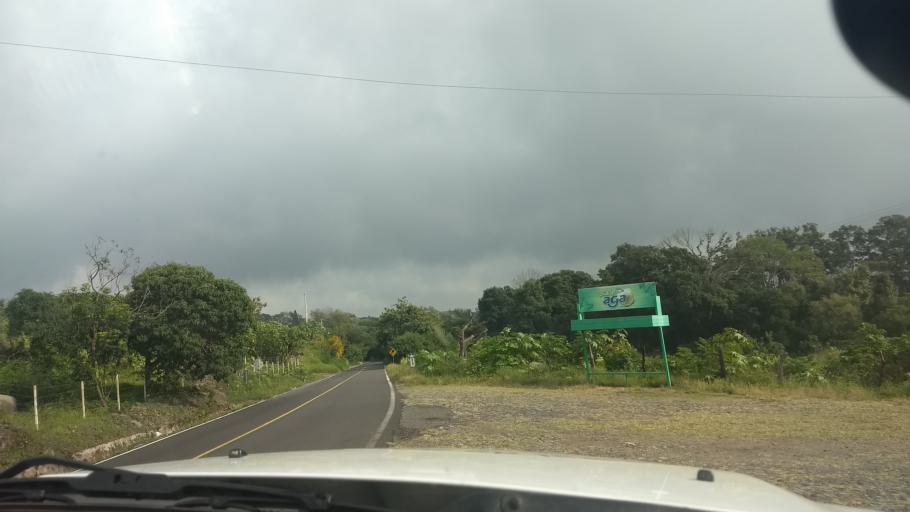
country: MX
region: Colima
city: Queseria
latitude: 19.4049
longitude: -103.6189
